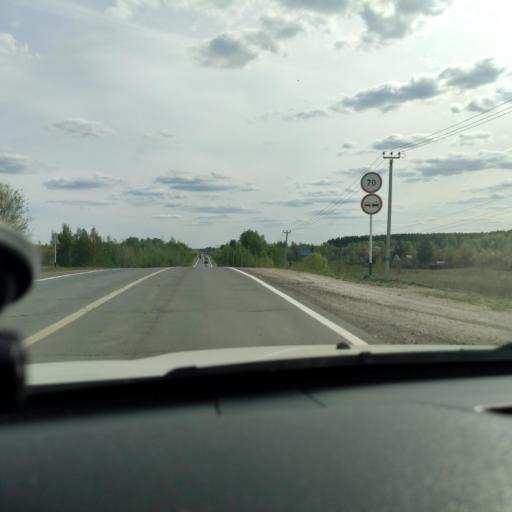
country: RU
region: Samara
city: Kinel'
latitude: 53.1914
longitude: 50.6394
